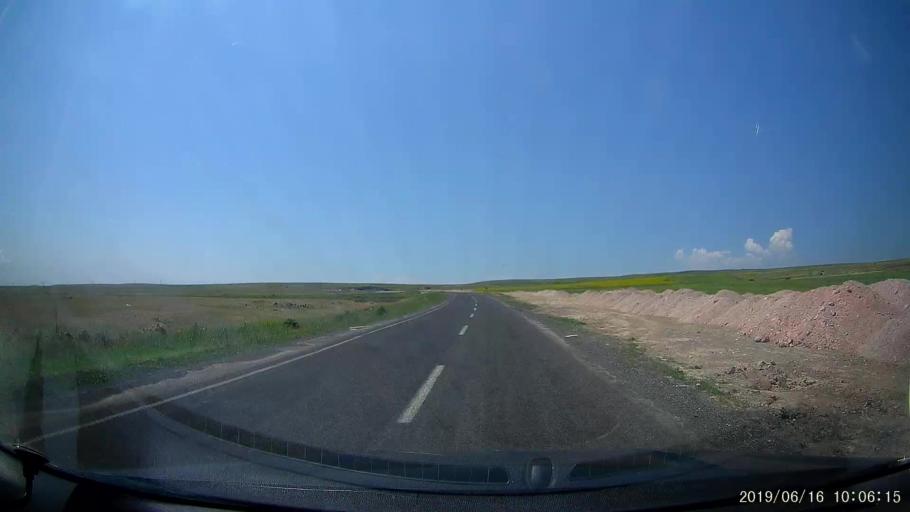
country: TR
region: Kars
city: Digor
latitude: 40.2575
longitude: 43.5412
